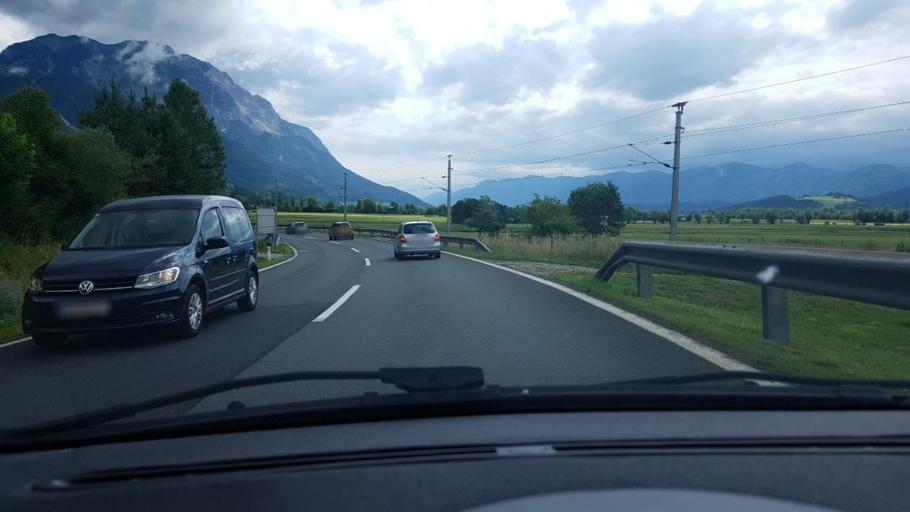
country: AT
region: Carinthia
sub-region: Politischer Bezirk Villach Land
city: Feistritz an der Gail
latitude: 46.5955
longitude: 13.5728
